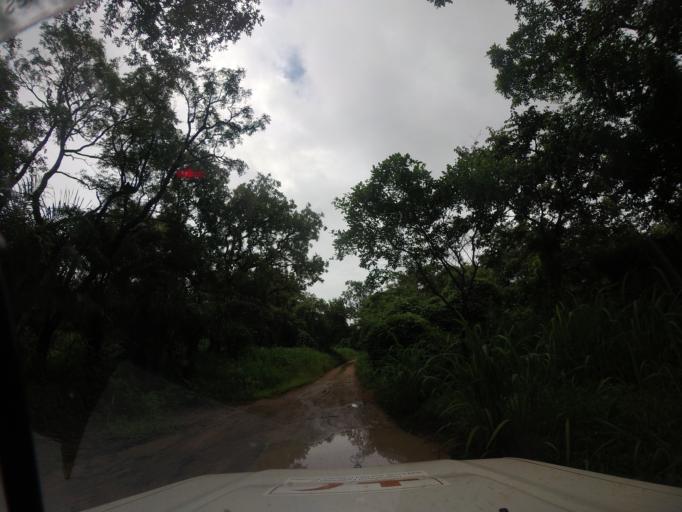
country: SL
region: Northern Province
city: Kamakwie
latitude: 9.6540
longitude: -12.2205
